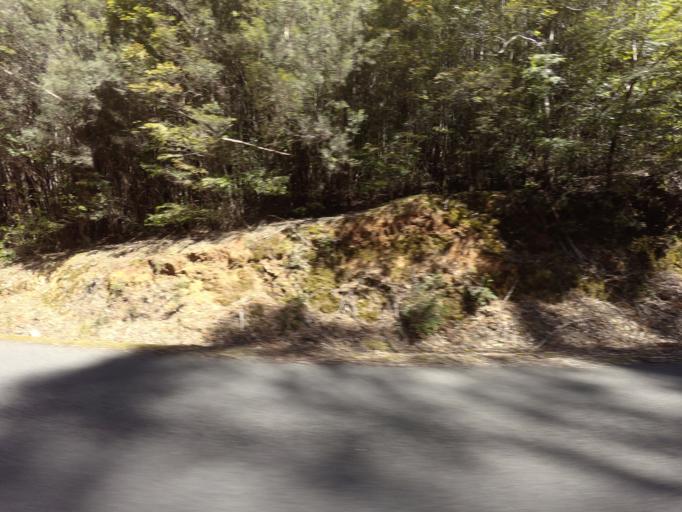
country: AU
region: Tasmania
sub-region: Huon Valley
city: Geeveston
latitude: -42.8189
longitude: 146.2874
